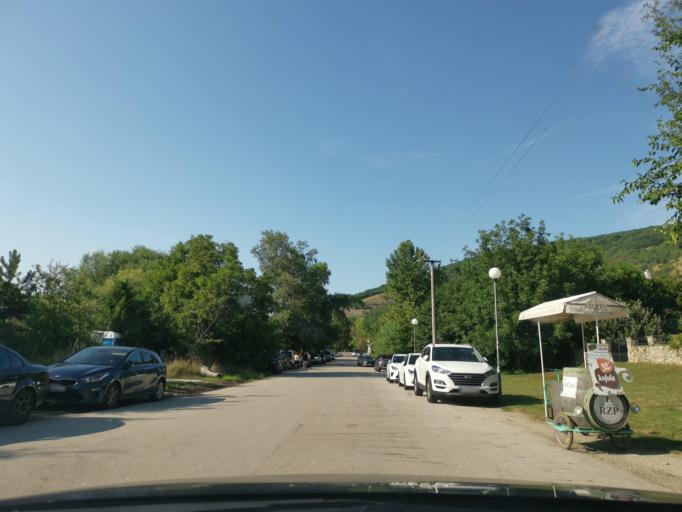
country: AT
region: Lower Austria
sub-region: Politischer Bezirk Bruck an der Leitha
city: Hainburg an der Donau
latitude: 48.1768
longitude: 16.9802
